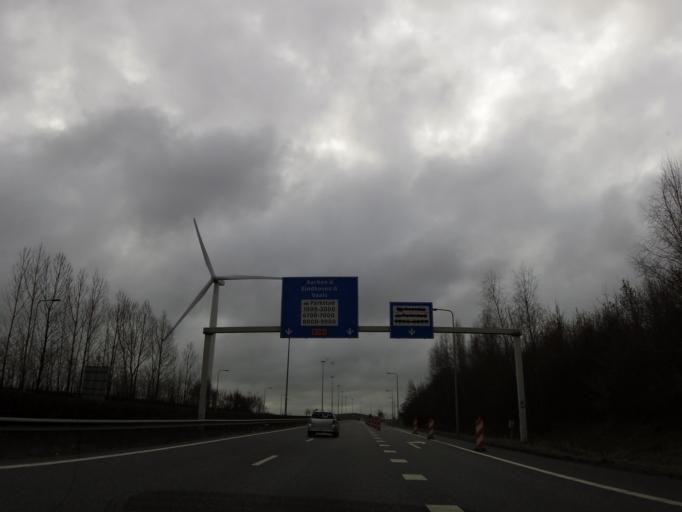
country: NL
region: Limburg
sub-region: Gemeente Simpelveld
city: Simpelveld
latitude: 50.8466
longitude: 6.0111
